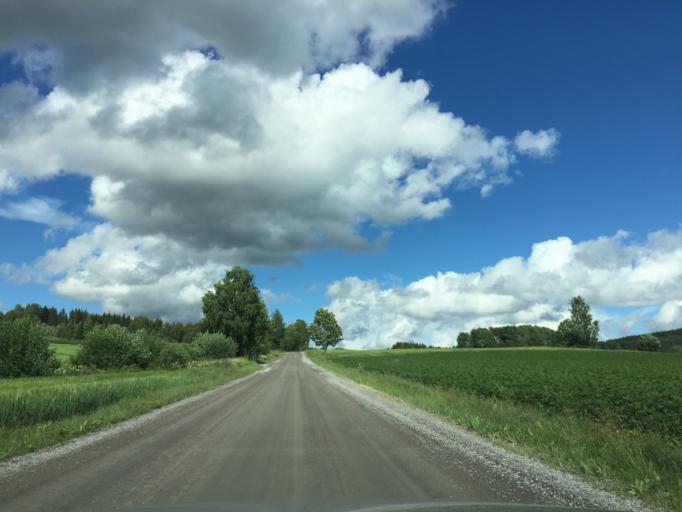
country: NO
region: Hedmark
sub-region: Kongsvinger
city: Spetalen
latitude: 60.2464
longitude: 11.8483
